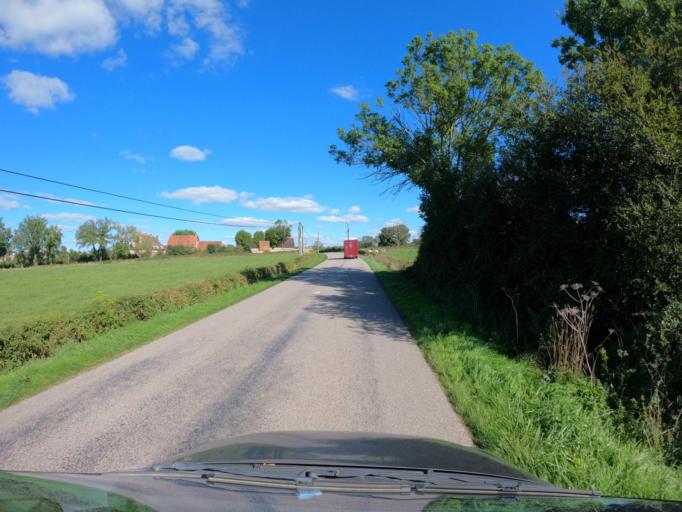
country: FR
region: Auvergne
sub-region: Departement de l'Allier
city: Buxieres-les-Mines
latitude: 46.4027
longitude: 2.9385
